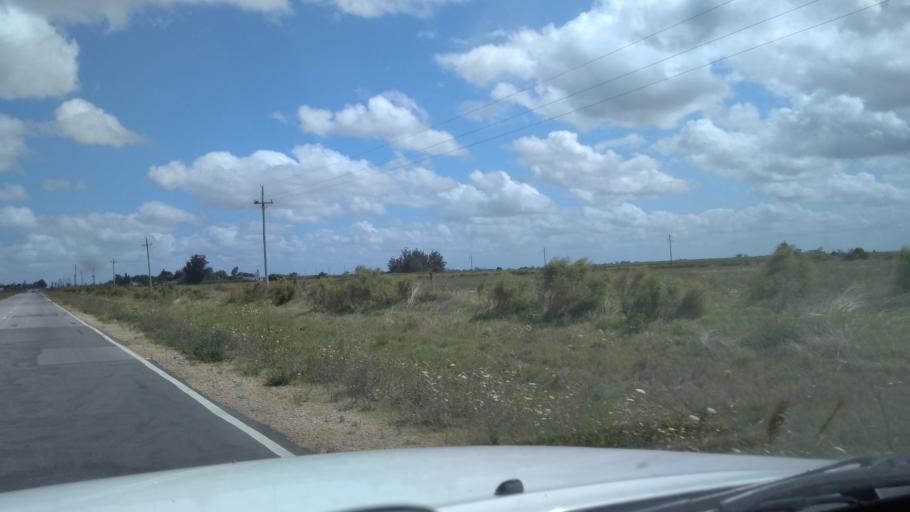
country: UY
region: Canelones
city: Santa Rosa
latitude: -34.5141
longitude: -56.0542
